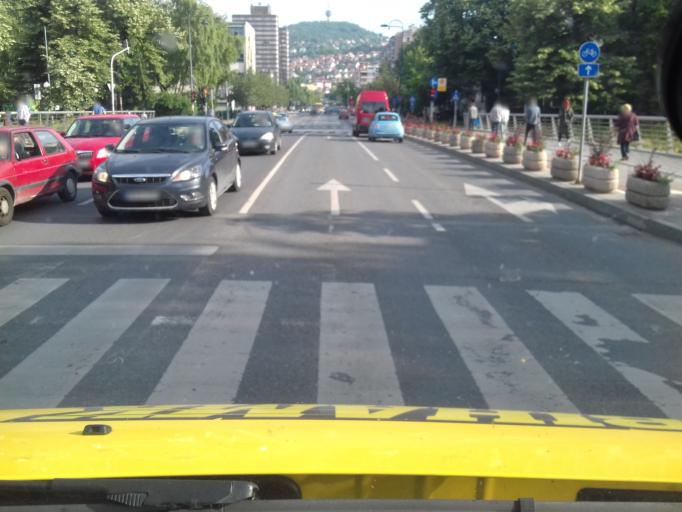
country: BA
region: Federation of Bosnia and Herzegovina
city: Kobilja Glava
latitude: 43.8525
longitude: 18.3932
